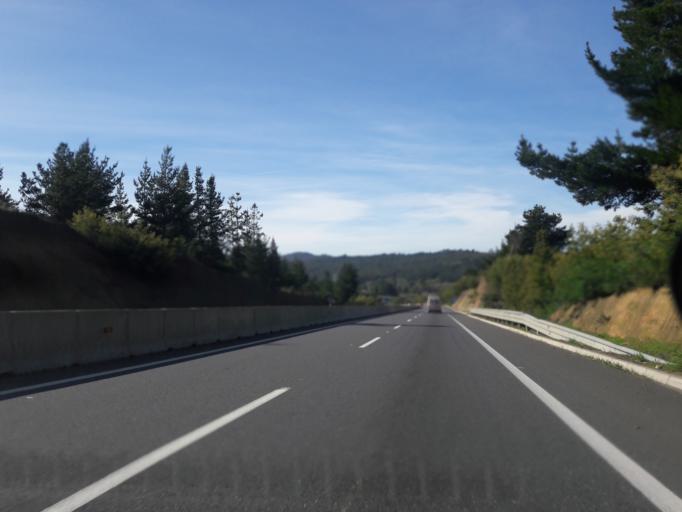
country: CL
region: Biobio
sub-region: Provincia de Biobio
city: Yumbel
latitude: -36.9779
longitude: -72.6465
